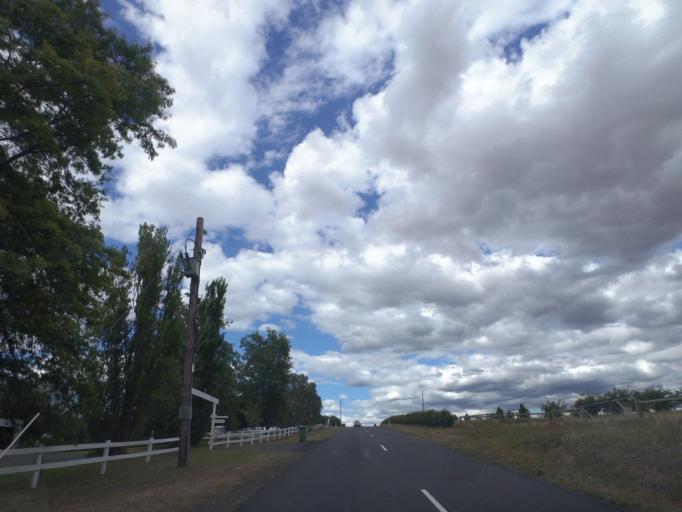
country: AU
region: Victoria
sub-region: Yarra Ranges
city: Yarra Glen
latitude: -37.6440
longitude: 145.4097
